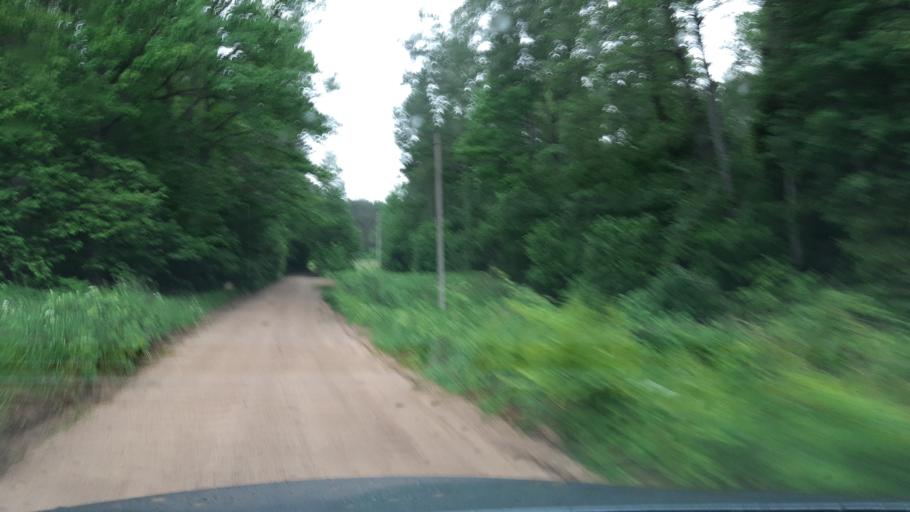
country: LT
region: Utenos apskritis
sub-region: Anyksciai
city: Anyksciai
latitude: 55.4504
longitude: 25.2113
